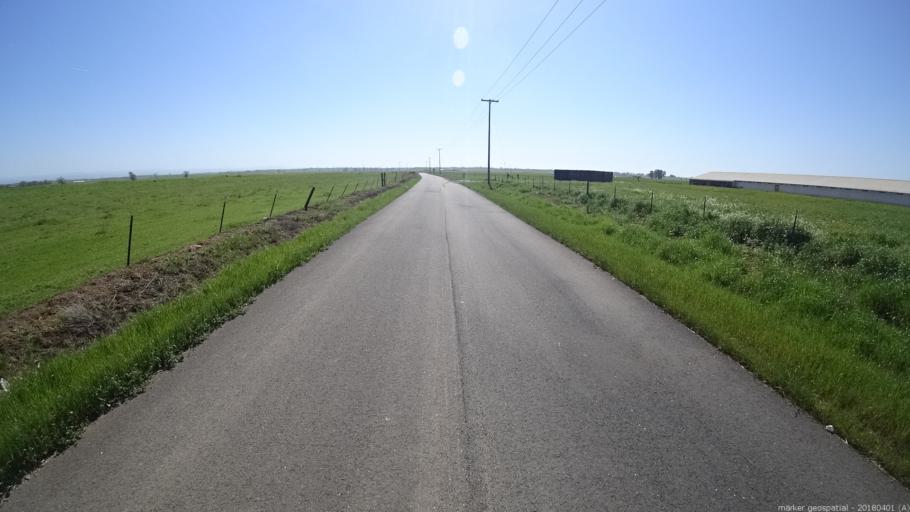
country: US
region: California
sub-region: Sacramento County
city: Rancho Murieta
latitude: 38.4682
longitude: -121.1603
